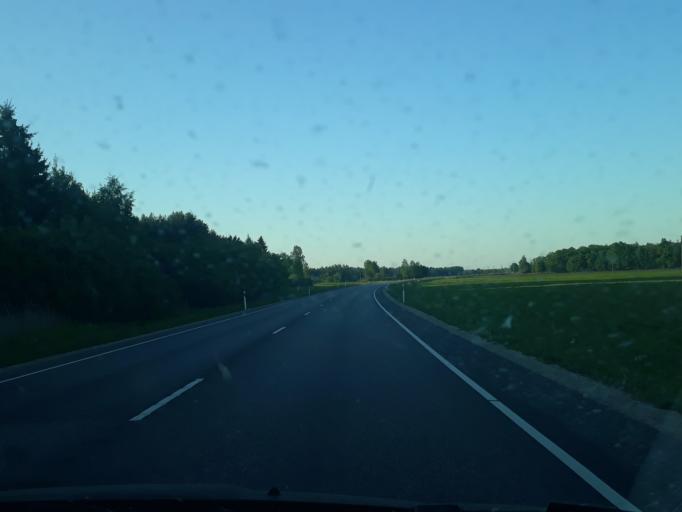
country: EE
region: Paernumaa
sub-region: Tootsi vald
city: Tootsi
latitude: 58.5683
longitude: 24.8742
